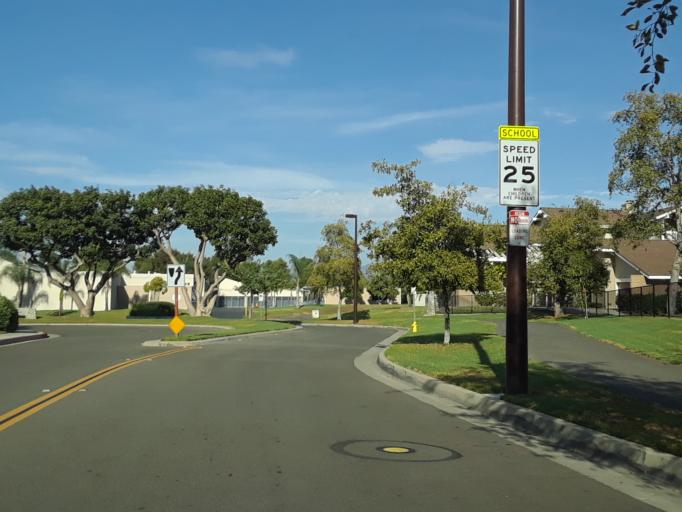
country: US
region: California
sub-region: Orange County
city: Irvine
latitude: 33.6833
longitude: -117.7961
